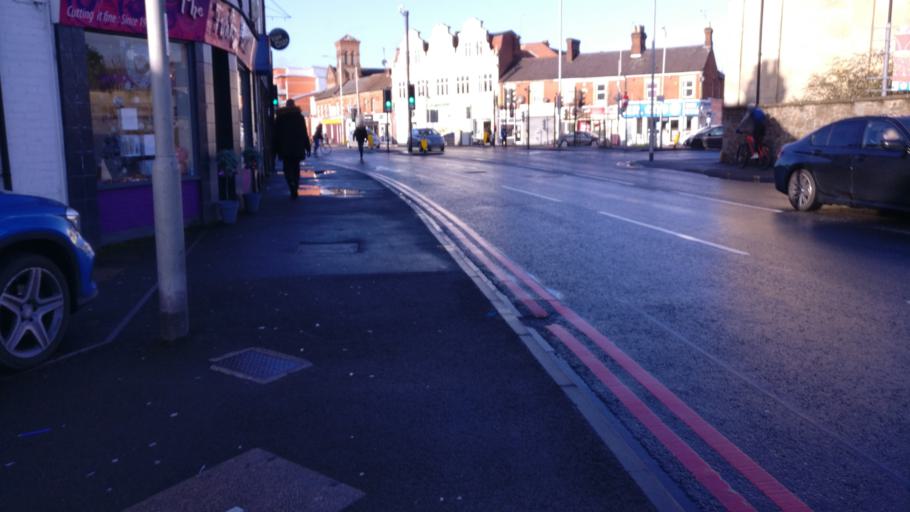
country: GB
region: England
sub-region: Reading
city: Reading
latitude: 51.4527
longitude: -0.9479
